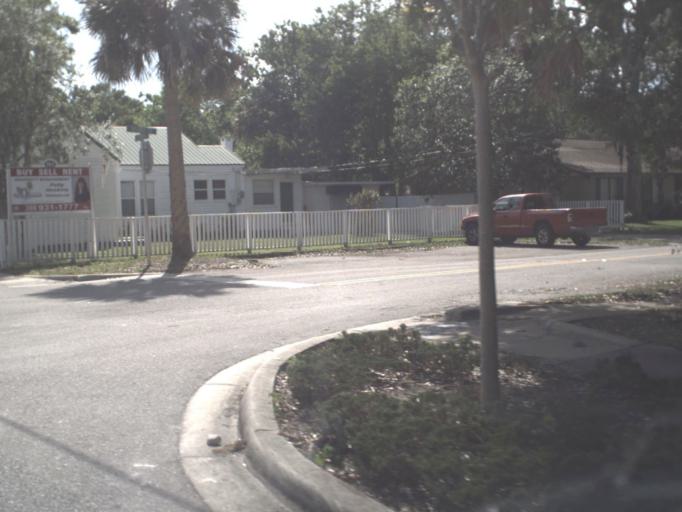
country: US
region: Florida
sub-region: Flagler County
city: Bunnell
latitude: 29.4708
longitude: -81.2530
